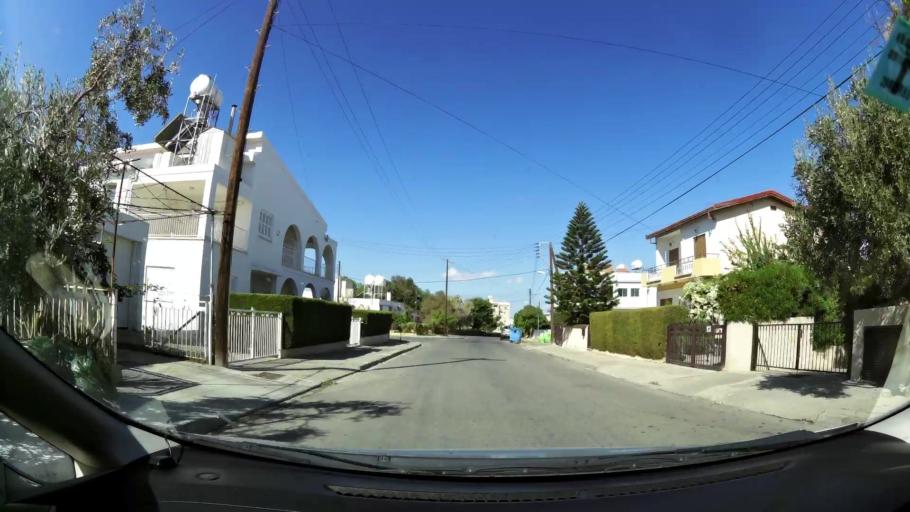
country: CY
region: Lefkosia
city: Nicosia
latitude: 35.1395
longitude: 33.3489
